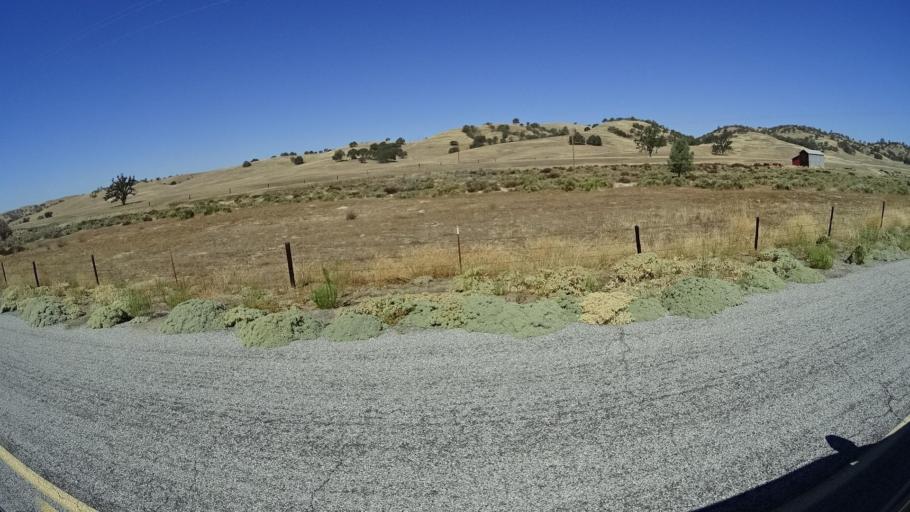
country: US
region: California
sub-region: San Luis Obispo County
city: San Miguel
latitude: 35.8263
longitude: -120.6449
